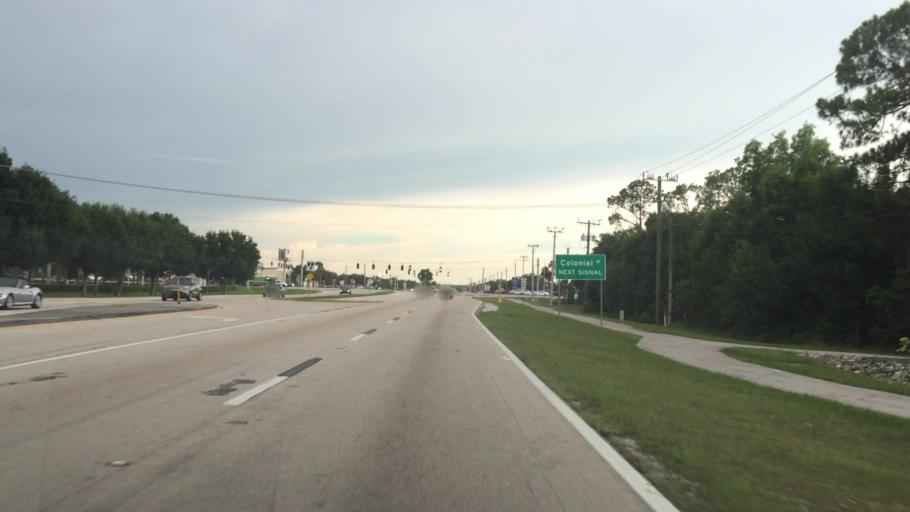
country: US
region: Florida
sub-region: Lee County
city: Fort Myers
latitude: 26.6150
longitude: -81.8114
